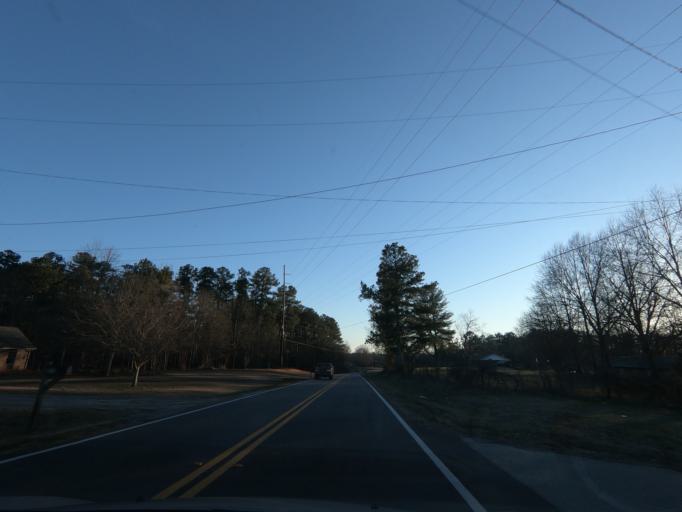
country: US
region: Georgia
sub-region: Forsyth County
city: Cumming
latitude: 34.3154
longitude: -84.1430
